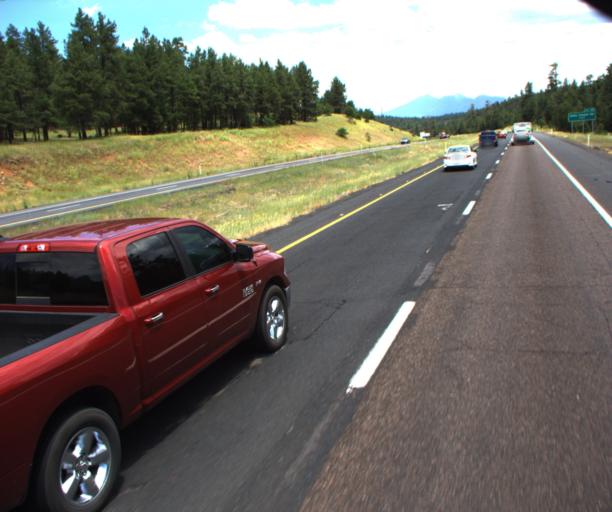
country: US
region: Arizona
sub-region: Coconino County
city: Mountainaire
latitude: 35.0304
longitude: -111.6843
